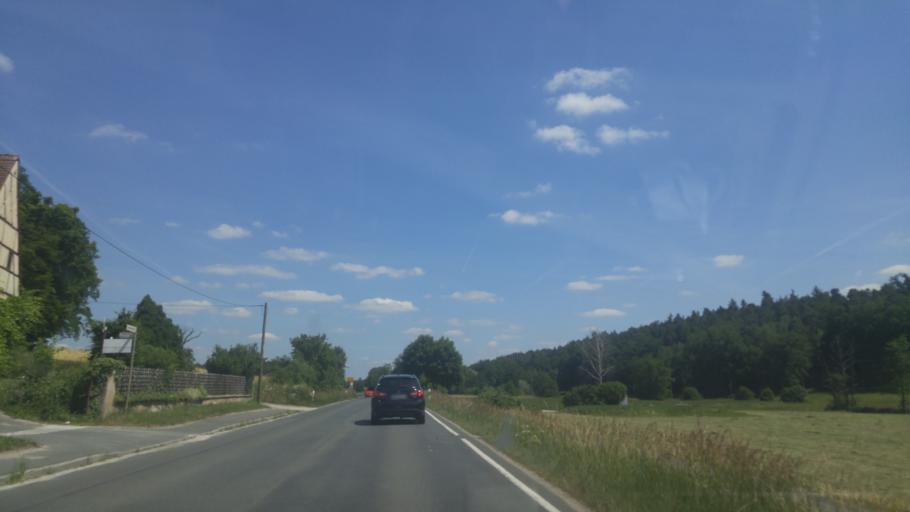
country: DE
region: Bavaria
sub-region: Regierungsbezirk Mittelfranken
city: Herzogenaurach
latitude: 49.5773
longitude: 10.8483
